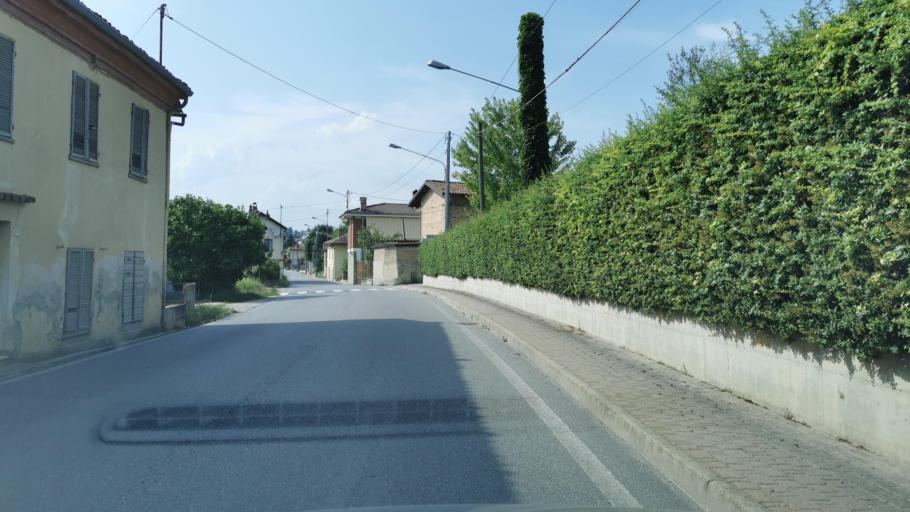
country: IT
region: Piedmont
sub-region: Provincia di Cuneo
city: Grinzane Cavour
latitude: 44.6446
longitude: 7.9987
